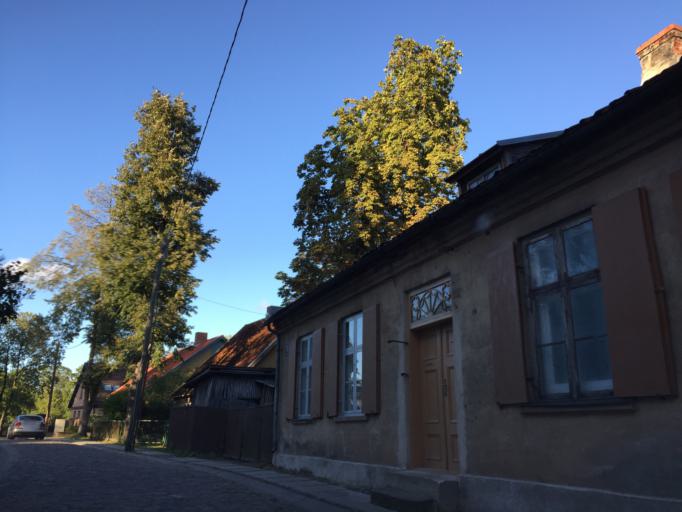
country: LV
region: Kuldigas Rajons
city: Kuldiga
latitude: 56.9669
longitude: 21.9734
